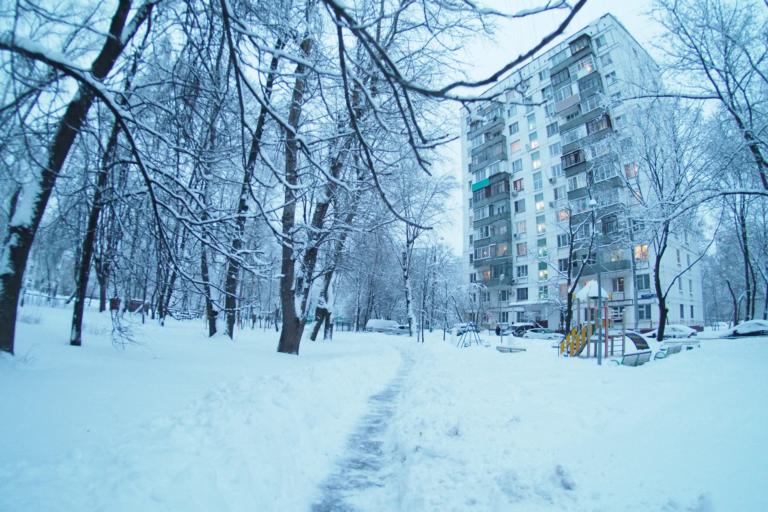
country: RU
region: Moscow
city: Perovo
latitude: 55.7422
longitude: 37.7836
